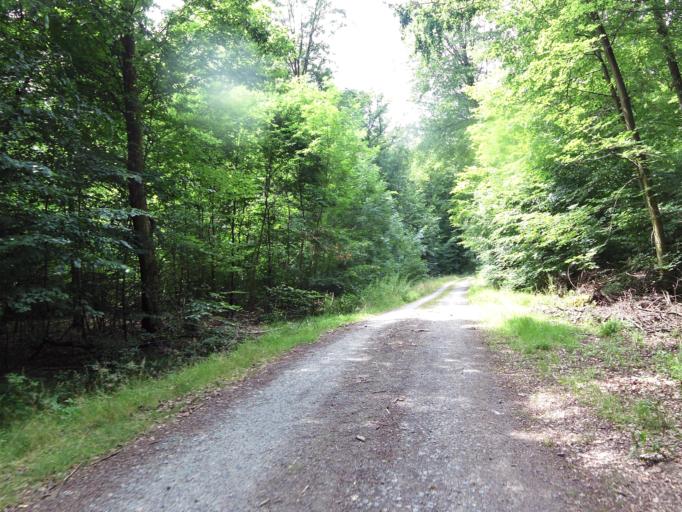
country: DE
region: Bavaria
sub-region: Regierungsbezirk Unterfranken
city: Wuerzburg
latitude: 49.7521
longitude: 9.8883
